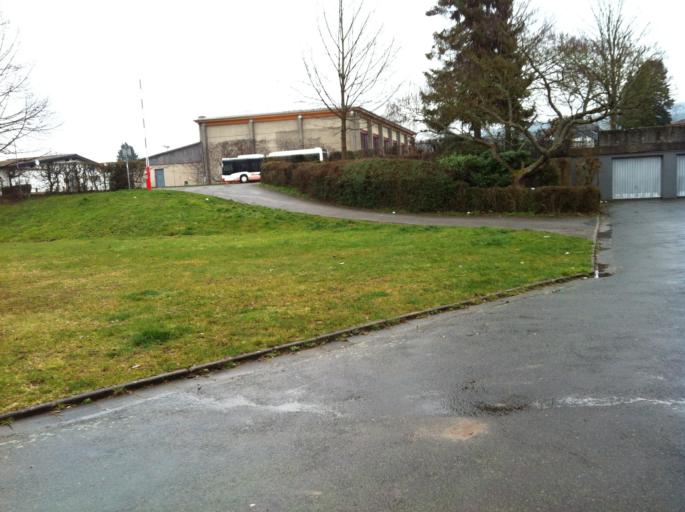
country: DE
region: Hesse
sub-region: Regierungsbezirk Darmstadt
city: Erbach
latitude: 49.6632
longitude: 9.0006
